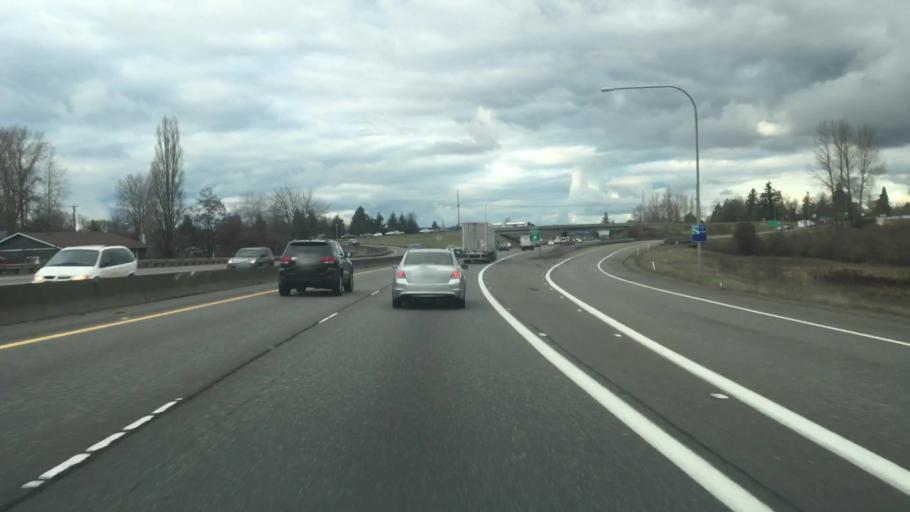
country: US
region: Washington
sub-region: Lewis County
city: Chehalis
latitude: 46.6570
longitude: -122.9773
